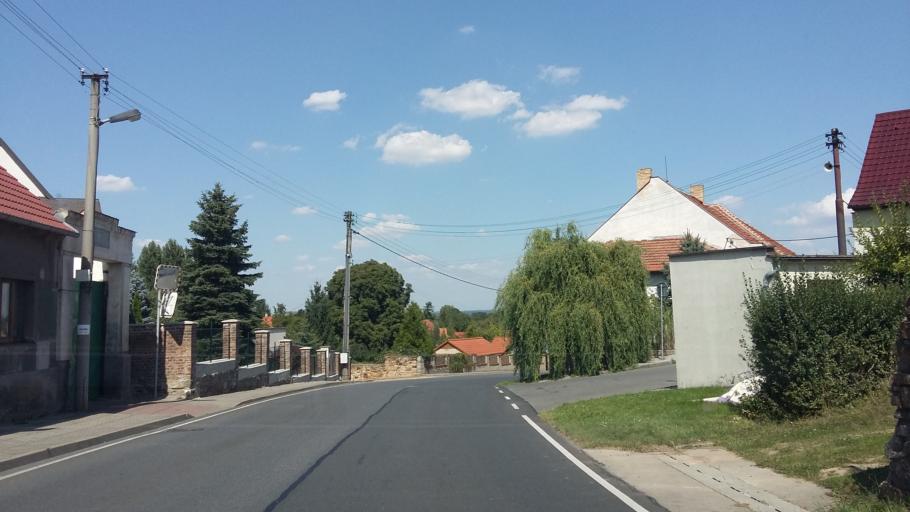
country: CZ
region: Central Bohemia
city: Brandys nad Labem-Stara Boleslav
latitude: 50.1628
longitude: 14.6809
